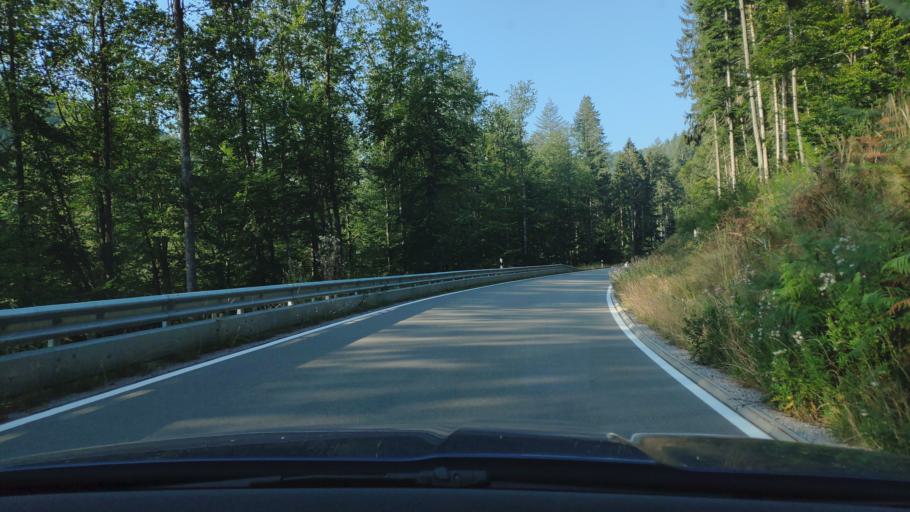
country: DE
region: Rheinland-Pfalz
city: Eppenbrunn
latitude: 49.0981
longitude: 7.6042
